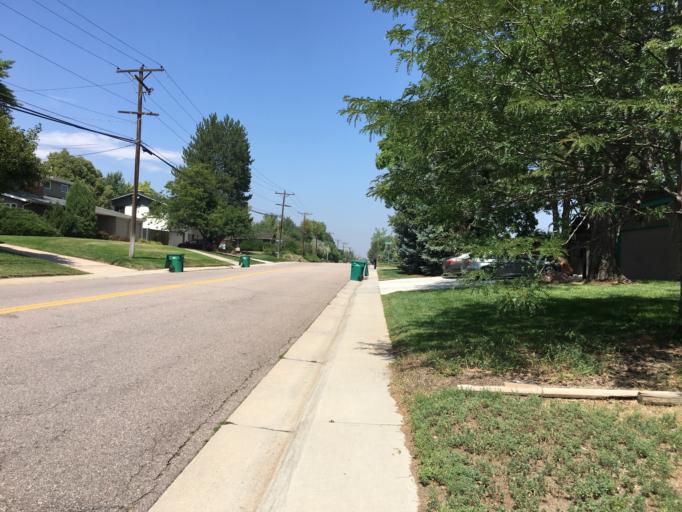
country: US
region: Colorado
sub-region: Arapahoe County
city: Glendale
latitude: 39.6715
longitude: -104.9222
